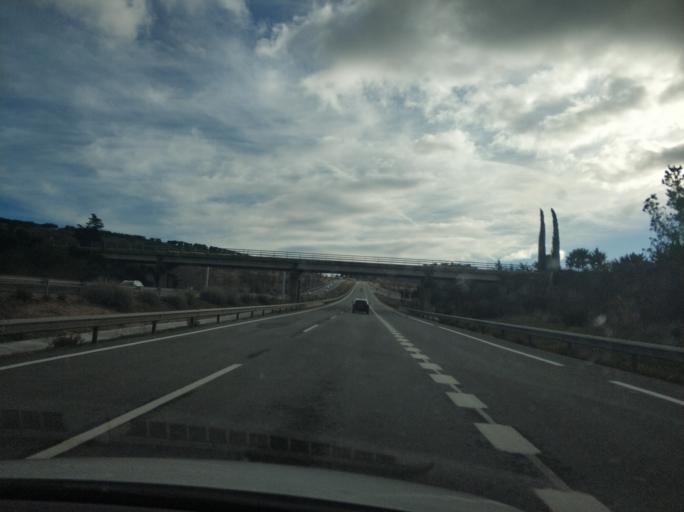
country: ES
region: Madrid
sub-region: Provincia de Madrid
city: Buitrago del Lozoya
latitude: 40.9649
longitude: -3.6417
